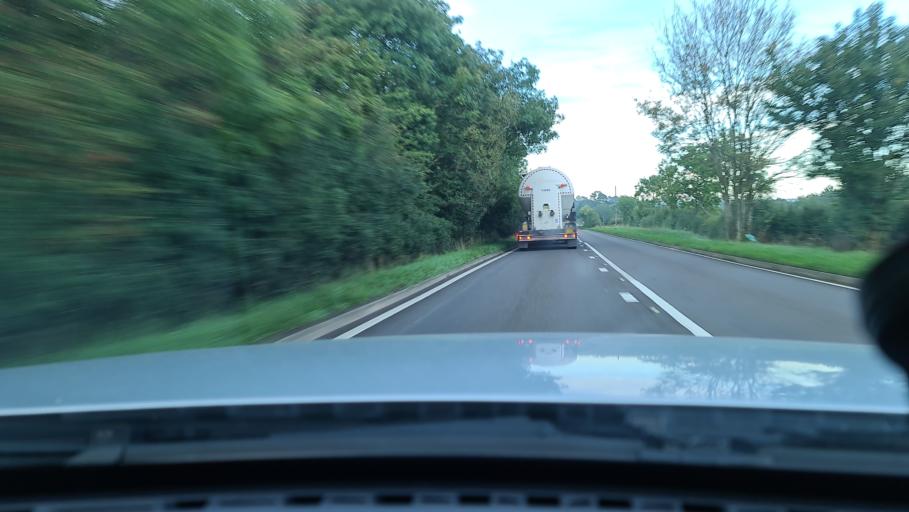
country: GB
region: England
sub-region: Oxfordshire
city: Claydon
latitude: 52.1703
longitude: -1.3649
